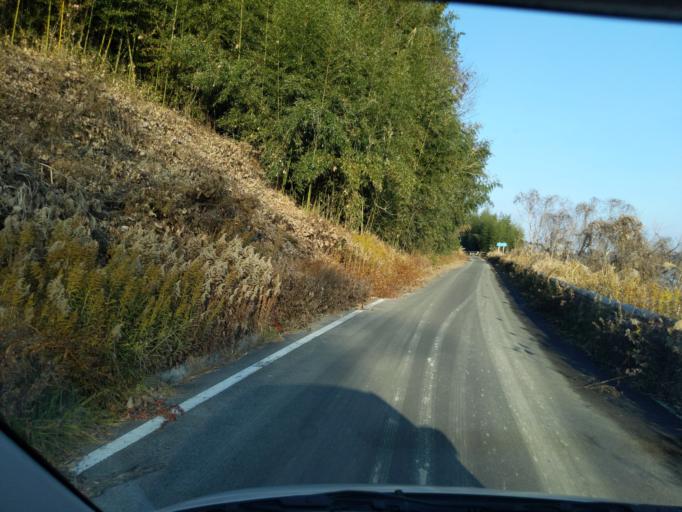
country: JP
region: Miyagi
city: Wakuya
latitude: 38.6979
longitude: 141.1274
